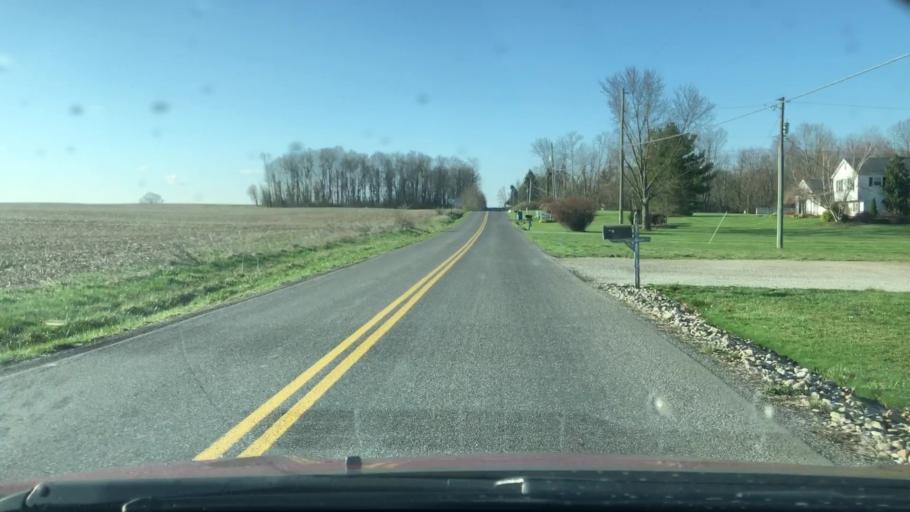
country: US
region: Ohio
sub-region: Wayne County
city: Wooster
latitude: 40.7835
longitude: -81.9067
